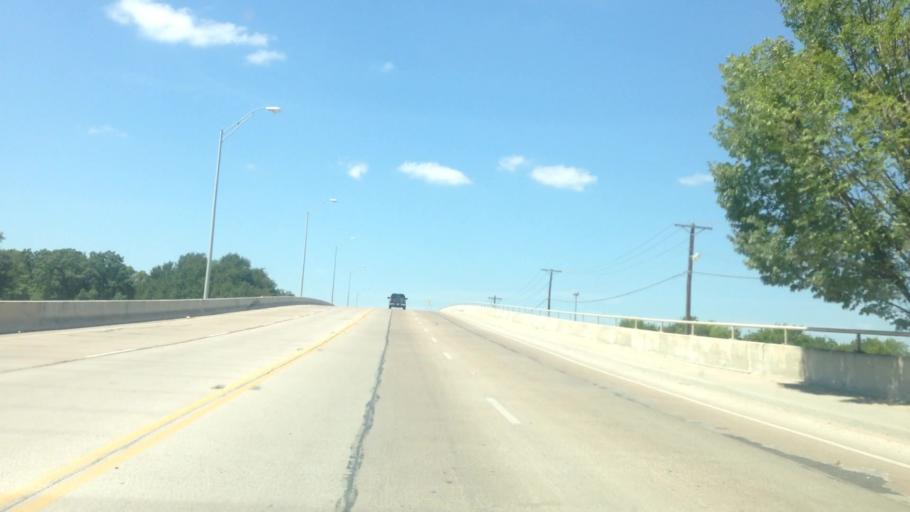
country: US
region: Texas
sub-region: Tarrant County
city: Haltom City
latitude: 32.7952
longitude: -97.3133
